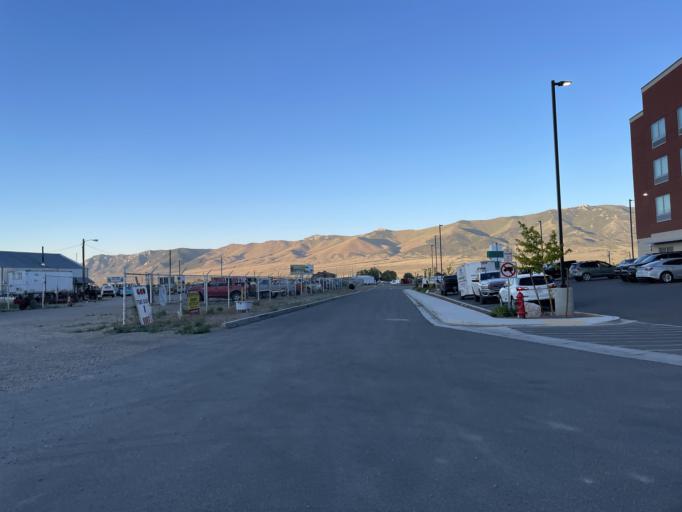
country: US
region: Nevada
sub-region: White Pine County
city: Ely
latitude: 39.2599
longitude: -114.8592
